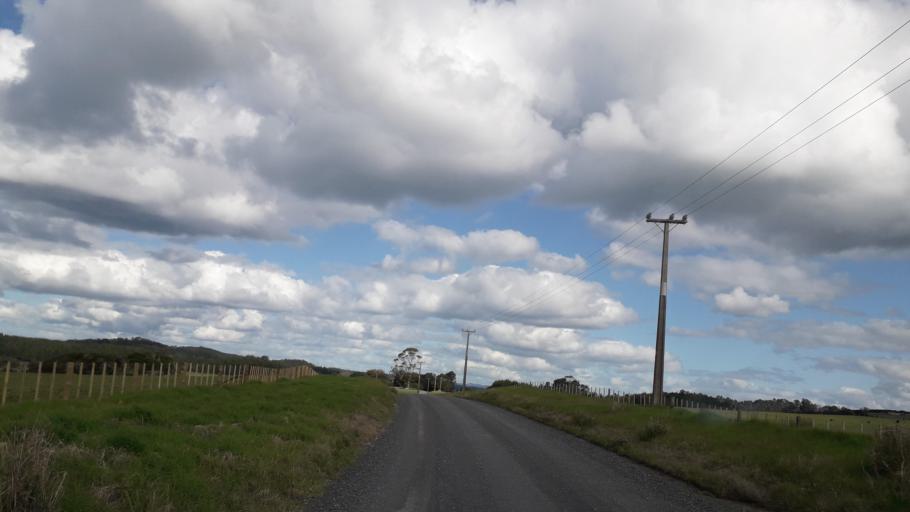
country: NZ
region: Northland
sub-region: Far North District
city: Kerikeri
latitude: -35.1475
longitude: 174.0380
